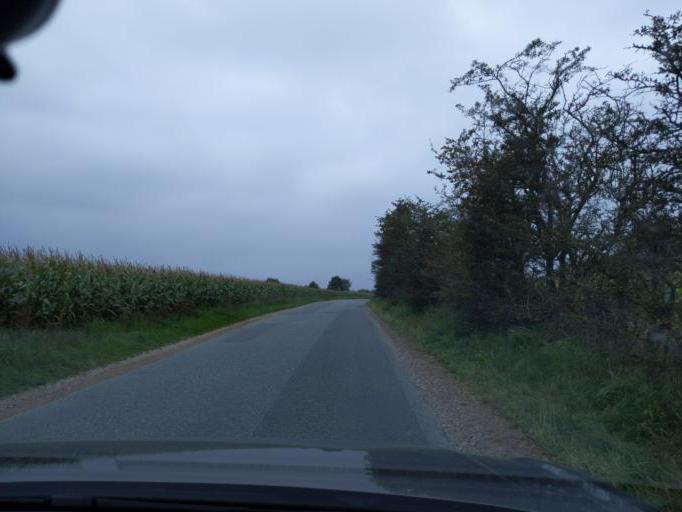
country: DK
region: Central Jutland
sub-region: Viborg Kommune
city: Stoholm
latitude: 56.5085
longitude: 9.2537
